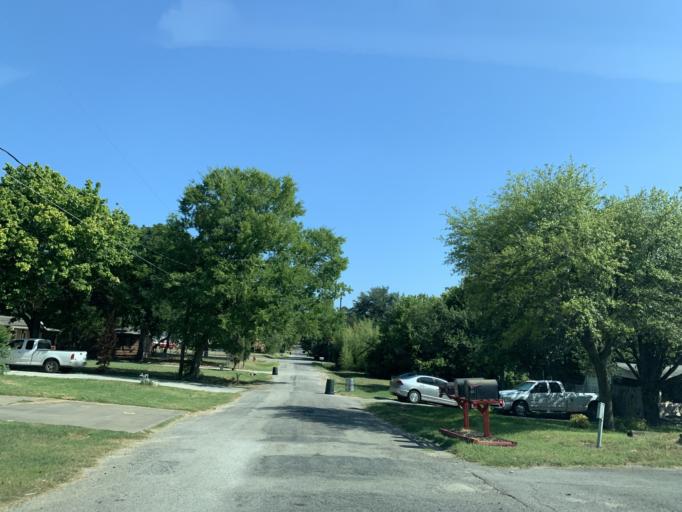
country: US
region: Texas
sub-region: Tarrant County
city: Azle
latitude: 32.8611
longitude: -97.5166
